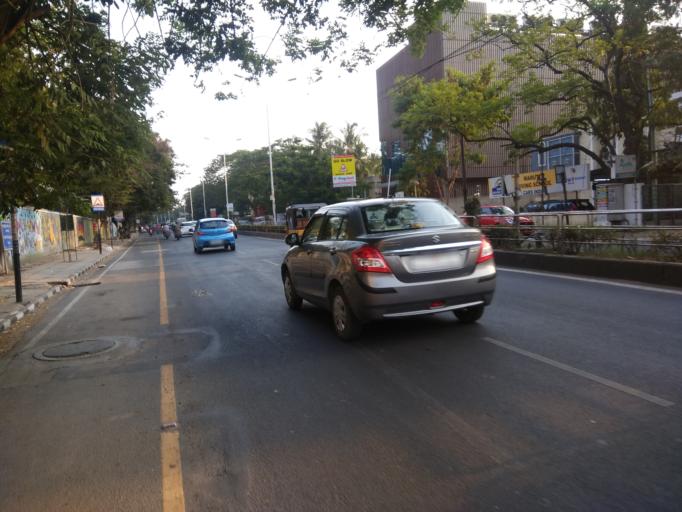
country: IN
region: Tamil Nadu
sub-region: Chennai
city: Gandhi Nagar
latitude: 13.0201
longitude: 80.2418
